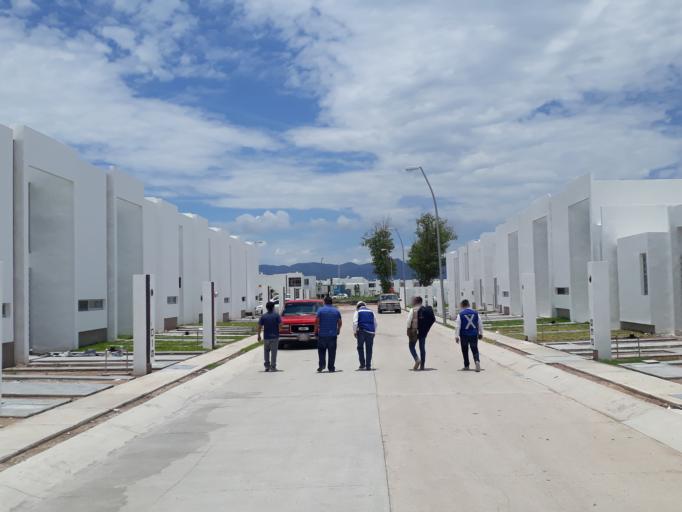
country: MX
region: Aguascalientes
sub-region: Aguascalientes
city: San Sebastian [Fraccionamiento]
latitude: 21.8311
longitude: -102.3168
